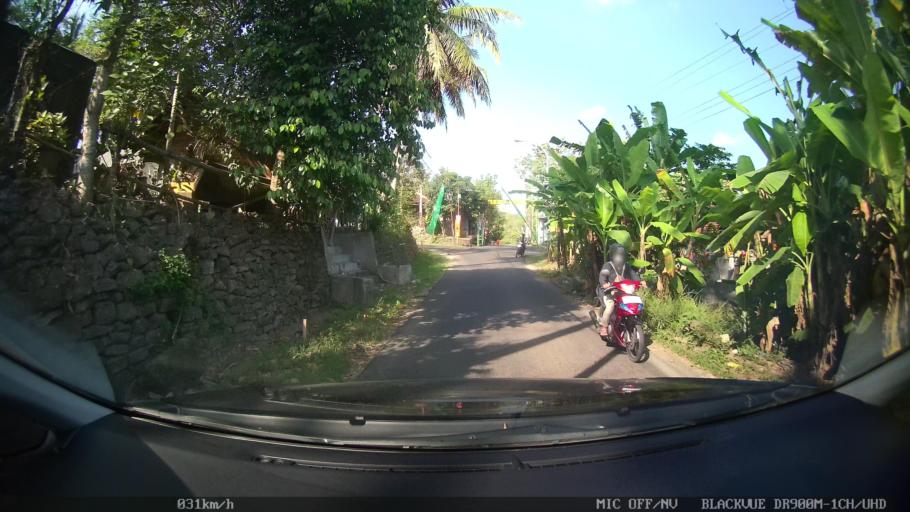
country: ID
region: Daerah Istimewa Yogyakarta
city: Kasihan
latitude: -7.8246
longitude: 110.2730
